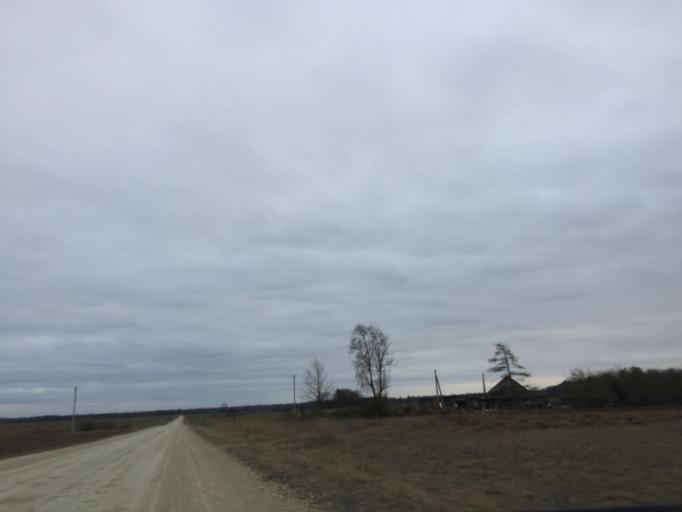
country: LT
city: Zagare
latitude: 56.3316
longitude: 23.2448
